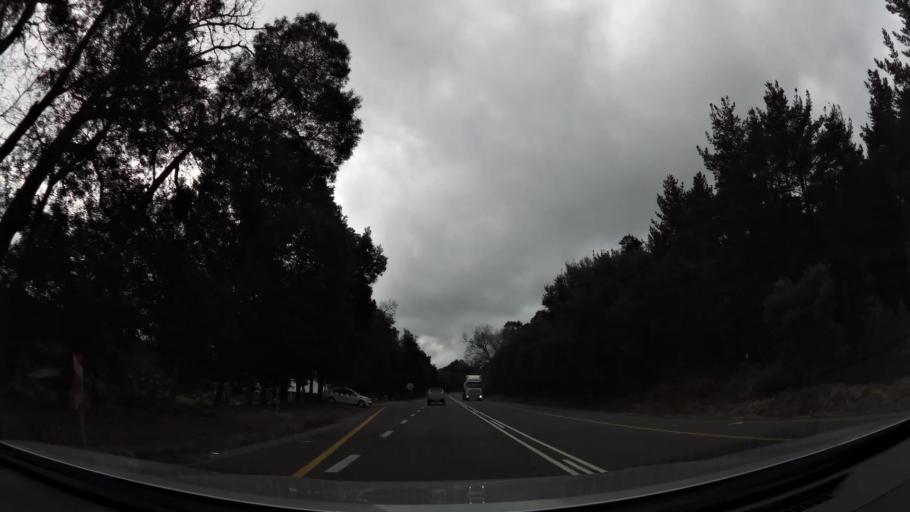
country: ZA
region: Western Cape
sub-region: Eden District Municipality
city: Knysna
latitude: -34.0284
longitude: 23.1593
